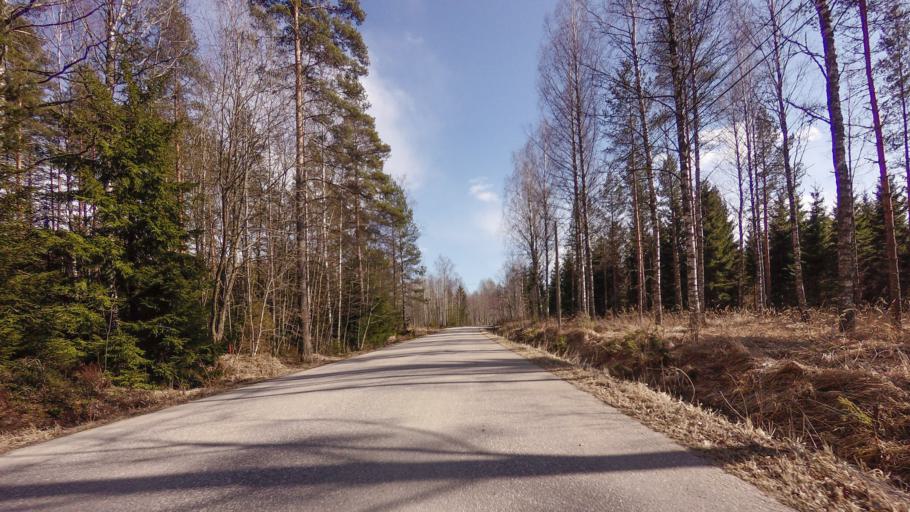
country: FI
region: Varsinais-Suomi
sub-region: Salo
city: Suomusjaervi
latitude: 60.3256
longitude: 23.6499
